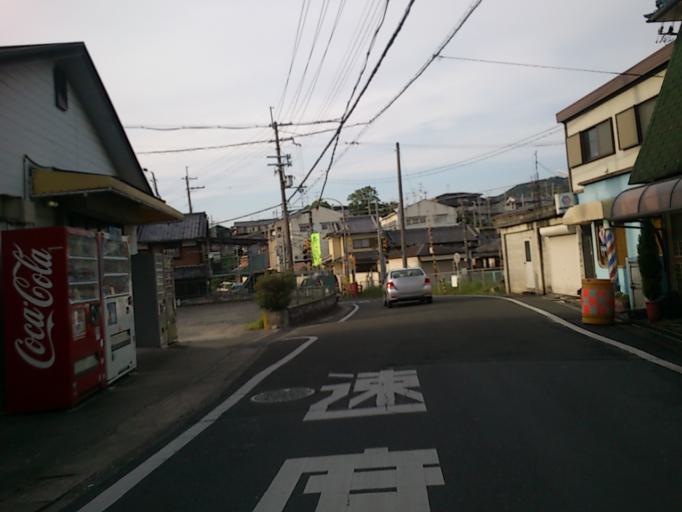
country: JP
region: Kyoto
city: Tanabe
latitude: 34.7914
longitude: 135.8102
